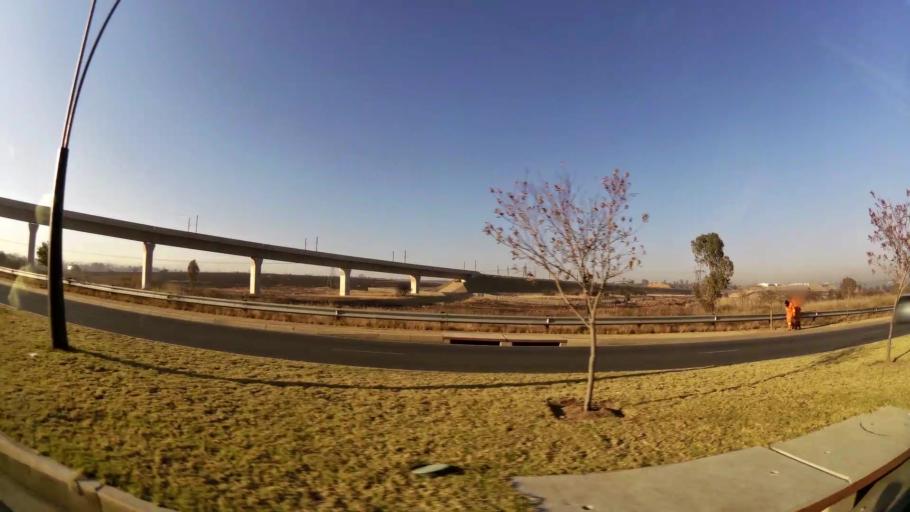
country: ZA
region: Gauteng
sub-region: City of Johannesburg Metropolitan Municipality
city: Midrand
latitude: -26.0264
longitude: 28.1264
